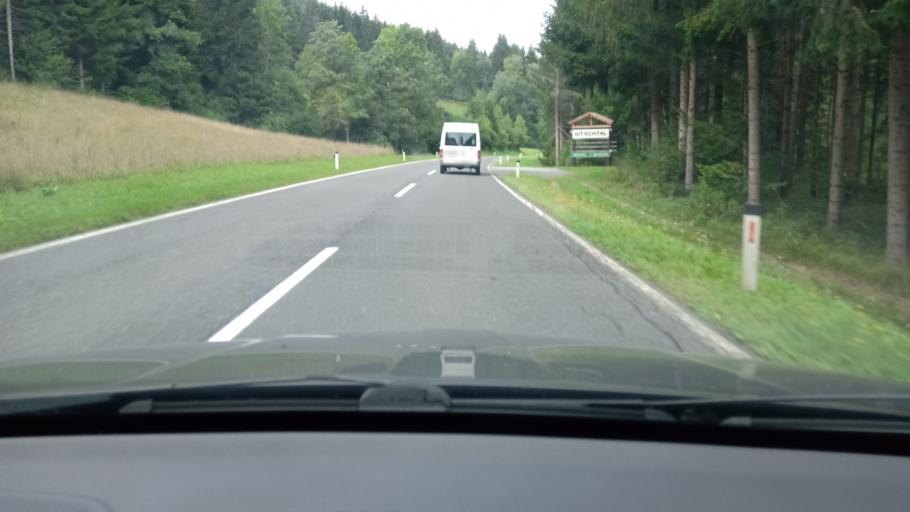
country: AT
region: Carinthia
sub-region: Politischer Bezirk Hermagor
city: Hermagor
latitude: 46.6488
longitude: 13.3308
